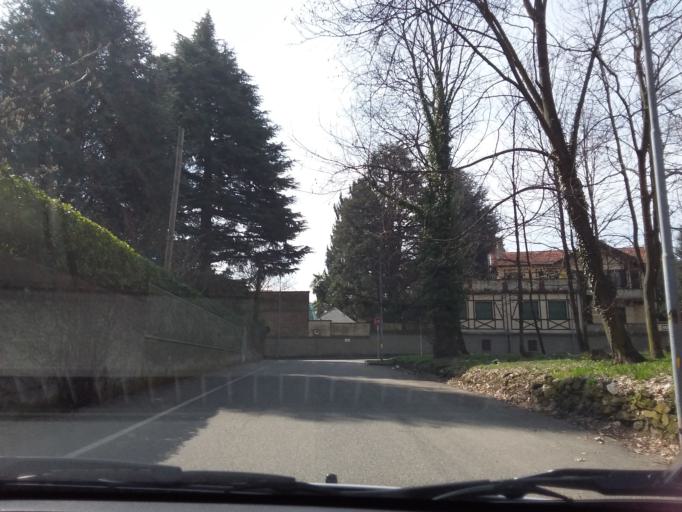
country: IT
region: Piedmont
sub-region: Provincia di Torino
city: Rivoli
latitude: 45.0696
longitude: 7.5285
